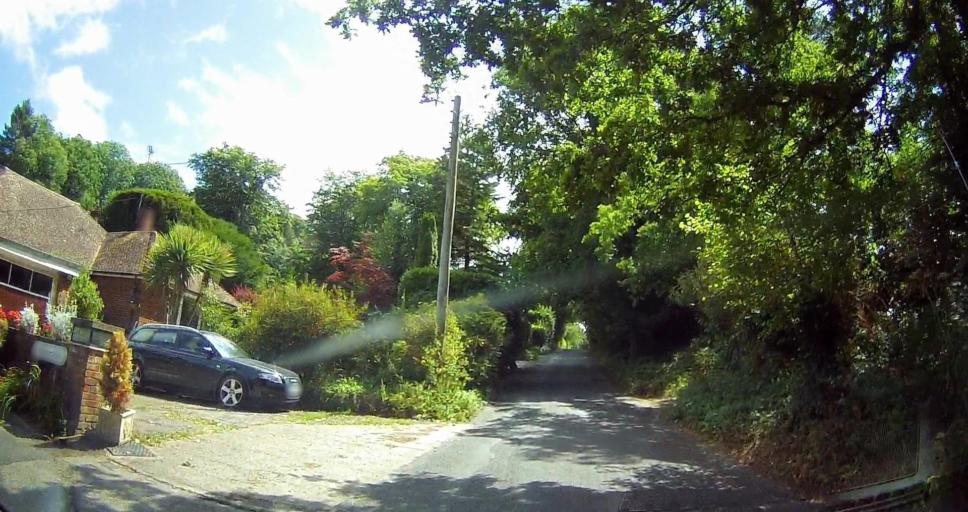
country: GB
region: England
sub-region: Kent
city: Borough Green
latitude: 51.2885
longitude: 0.3113
